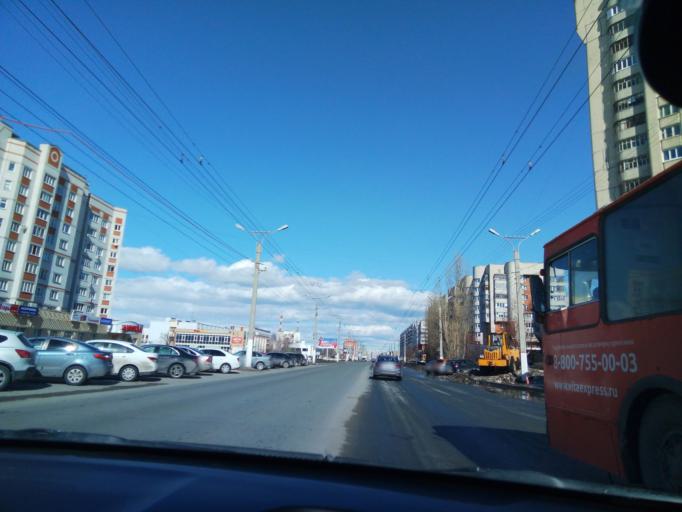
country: RU
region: Chuvashia
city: Novyye Lapsary
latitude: 56.1181
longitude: 47.1840
